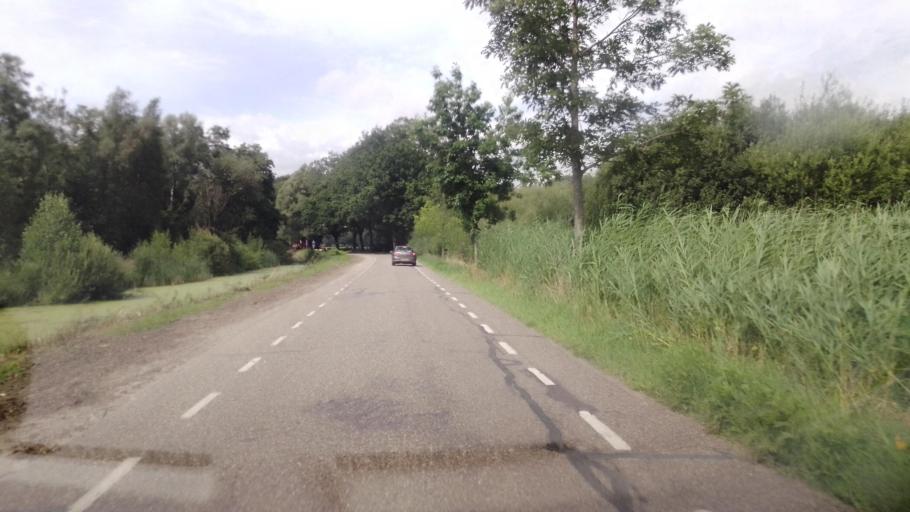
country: NL
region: Limburg
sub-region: Gemeente Venray
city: Venray
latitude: 51.4418
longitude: 5.9064
